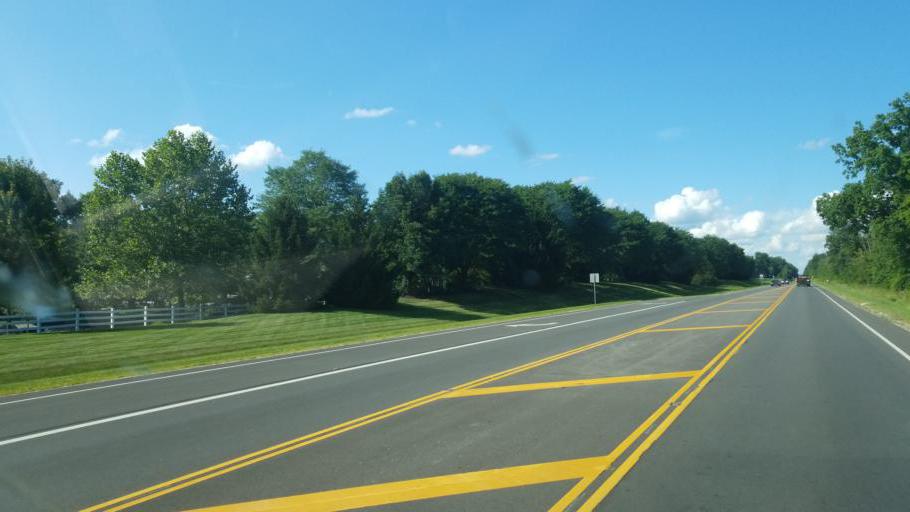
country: US
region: Ohio
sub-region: Franklin County
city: Westerville
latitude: 40.1580
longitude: -82.9188
